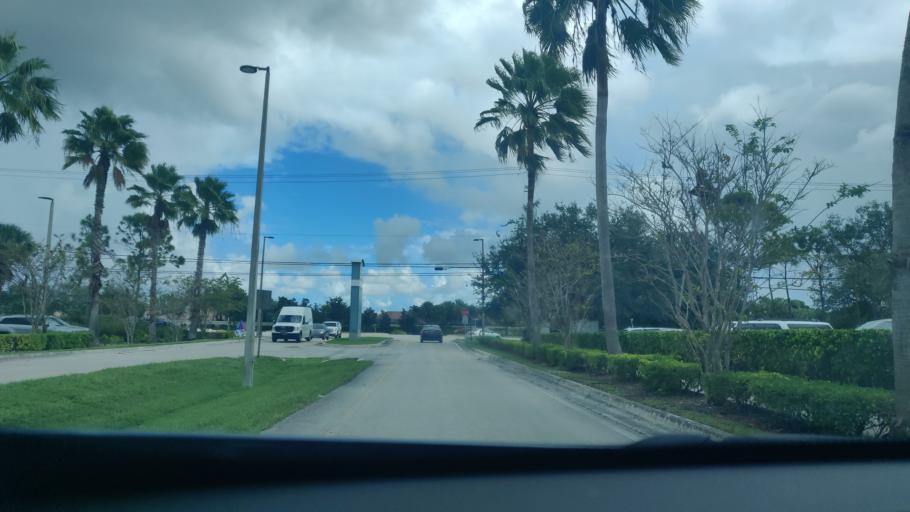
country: US
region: Florida
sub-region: Palm Beach County
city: Wellington
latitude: 26.6553
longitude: -80.2043
